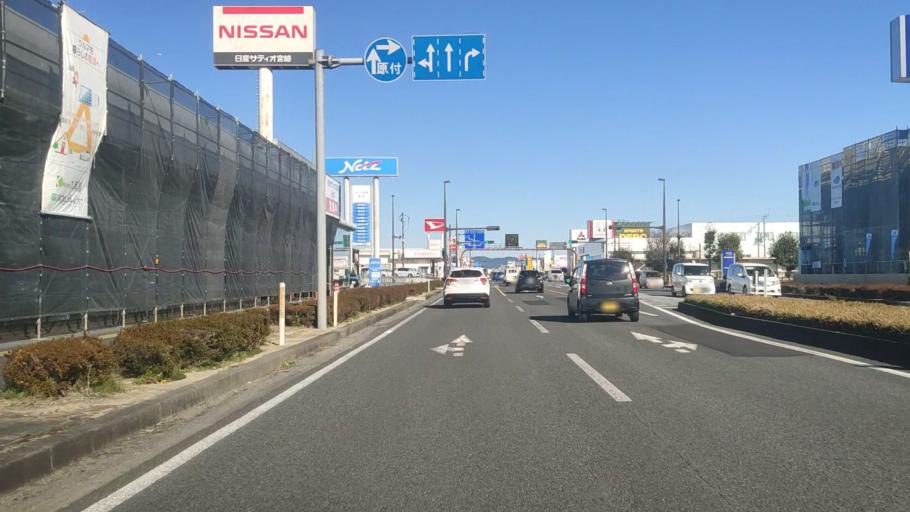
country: JP
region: Miyazaki
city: Miyakonojo
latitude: 31.7593
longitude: 131.0854
